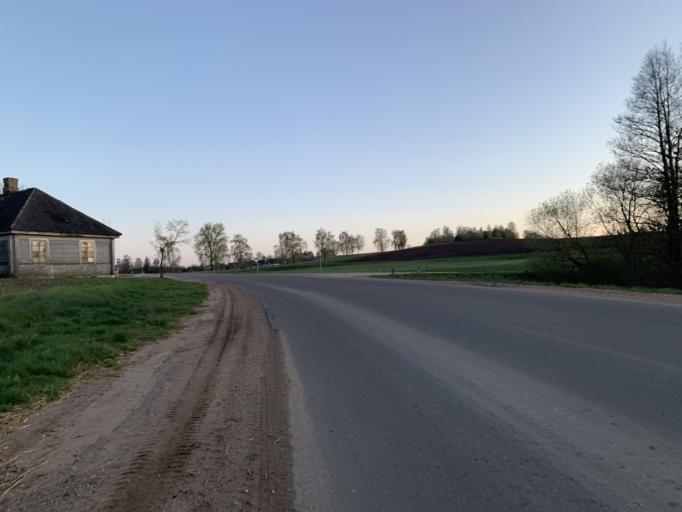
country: BY
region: Minsk
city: Haradzyeya
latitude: 53.2602
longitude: 26.5436
